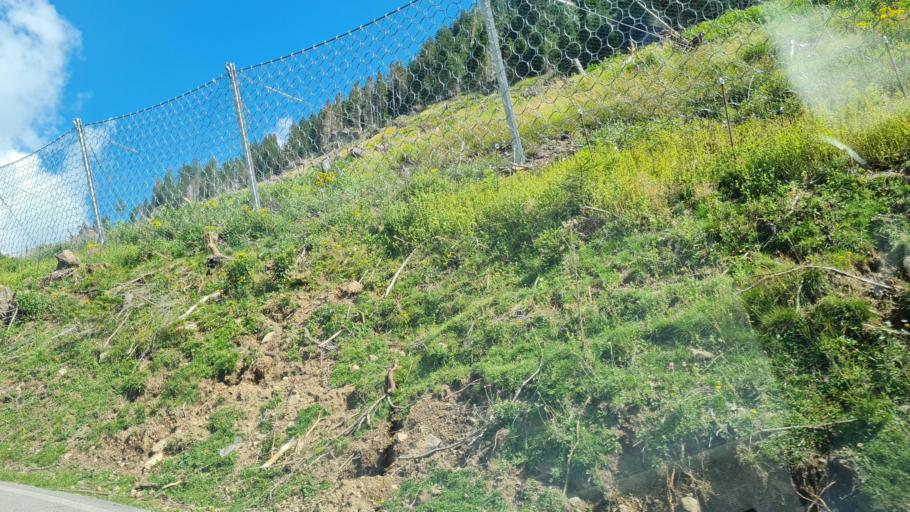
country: IT
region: Trentino-Alto Adige
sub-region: Provincia di Trento
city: Torcegno
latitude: 46.1528
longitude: 11.4426
